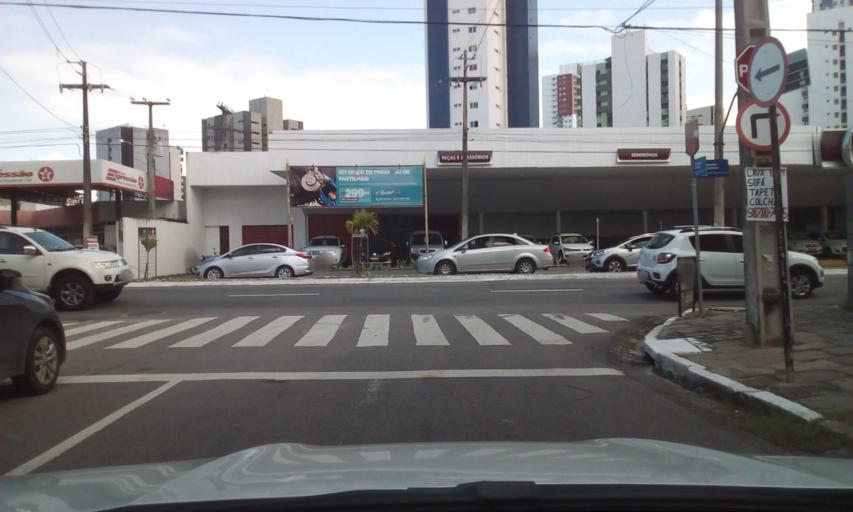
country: BR
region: Paraiba
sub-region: Joao Pessoa
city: Joao Pessoa
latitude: -7.1124
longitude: -34.8293
